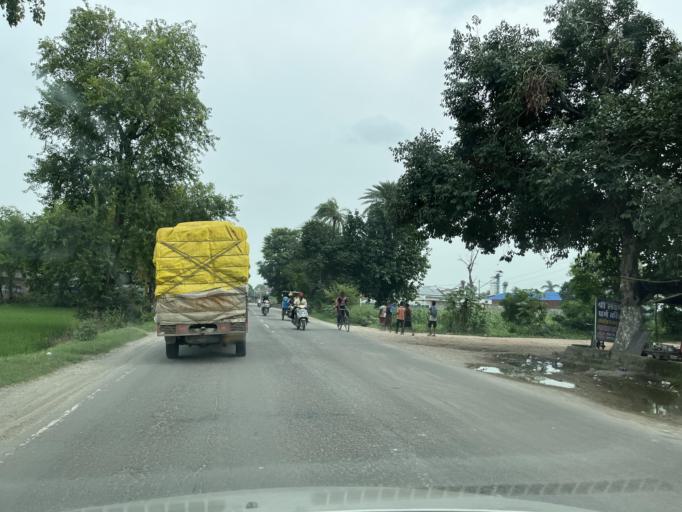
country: IN
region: Uttar Pradesh
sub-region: Rampur
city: Bilaspur
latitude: 29.0337
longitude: 79.2589
